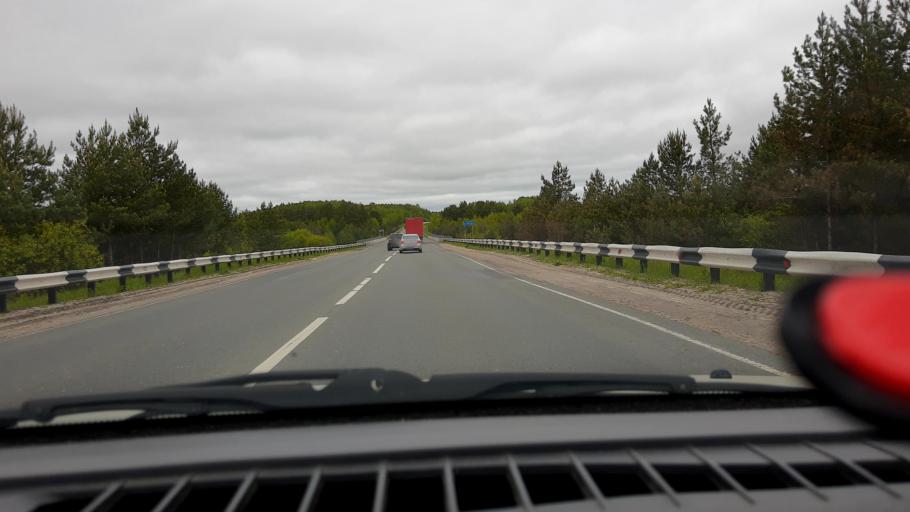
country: RU
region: Nizjnij Novgorod
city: Sitniki
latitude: 56.4758
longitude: 44.0289
